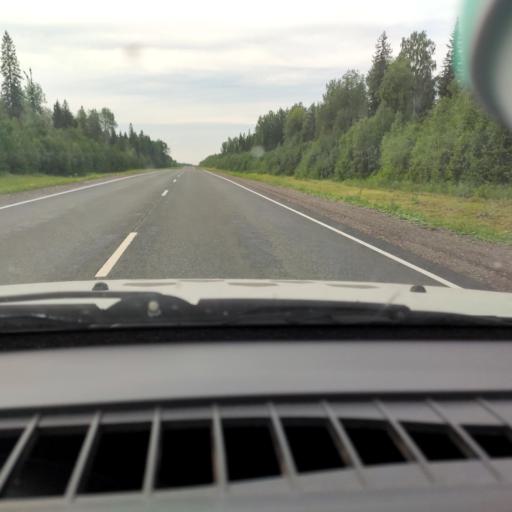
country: RU
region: Kirov
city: Kostino
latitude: 58.7666
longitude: 53.6097
